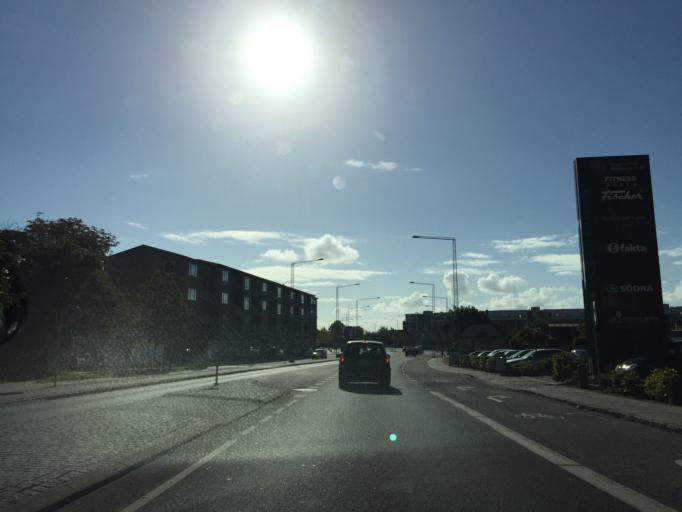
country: DK
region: Central Jutland
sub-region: Arhus Kommune
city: Arhus
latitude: 56.1687
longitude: 10.1617
